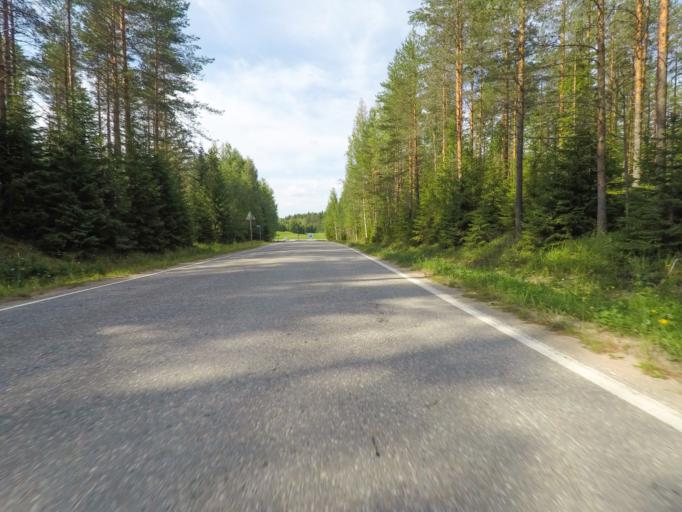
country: FI
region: Southern Savonia
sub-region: Savonlinna
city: Sulkava
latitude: 61.7890
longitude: 28.2431
